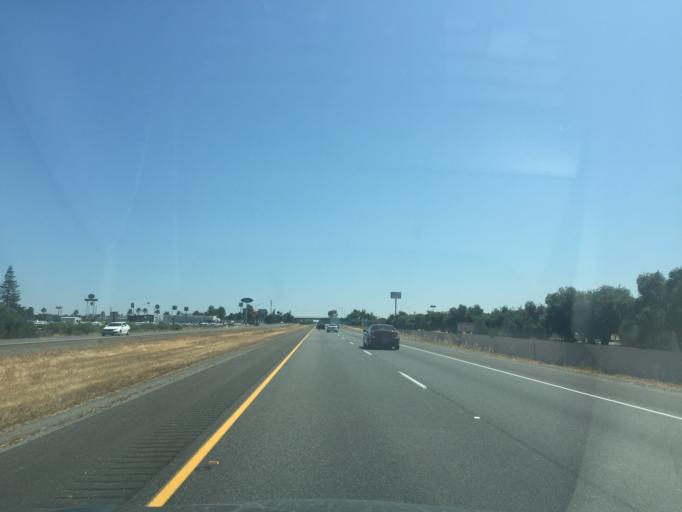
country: US
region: California
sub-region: Tehama County
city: Corning
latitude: 39.9352
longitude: -122.2004
